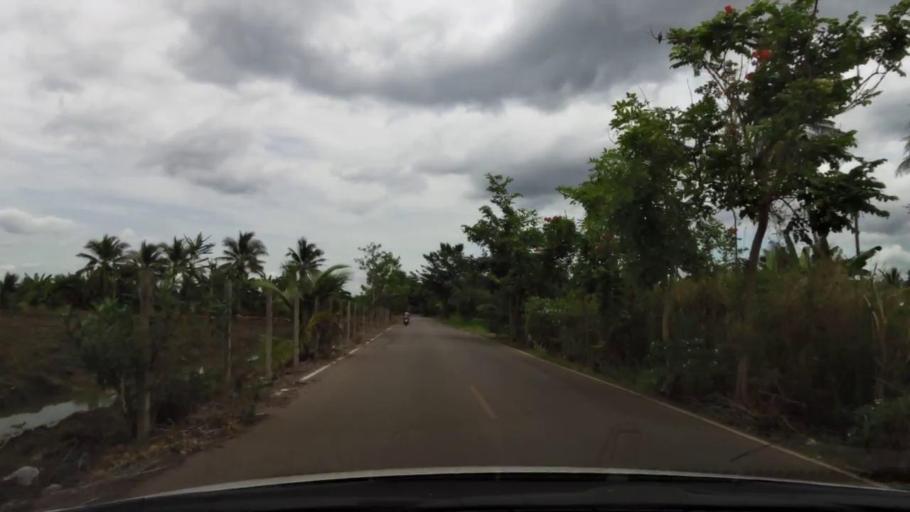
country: TH
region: Samut Sakhon
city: Ban Phaeo
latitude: 13.5645
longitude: 100.0336
